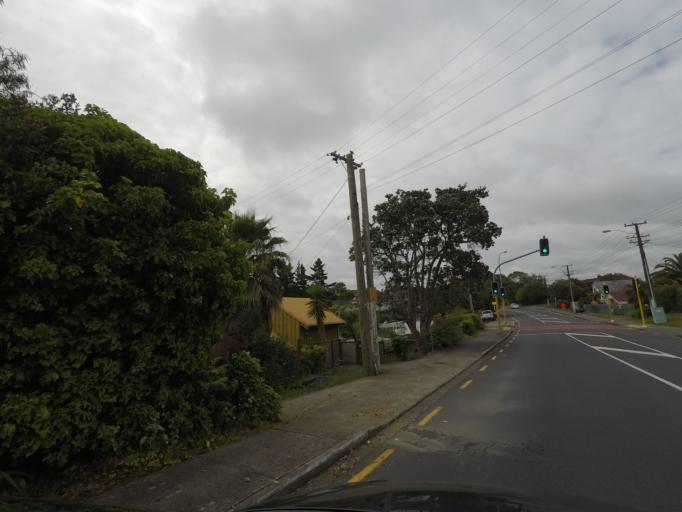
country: NZ
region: Auckland
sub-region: Auckland
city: Rosebank
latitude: -36.8398
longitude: 174.6004
